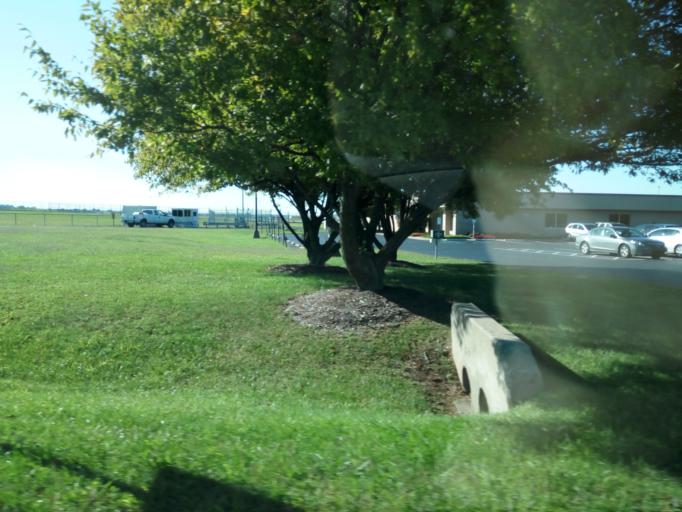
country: US
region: Kentucky
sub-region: Jefferson County
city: Audubon Park
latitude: 38.1884
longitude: -85.7366
